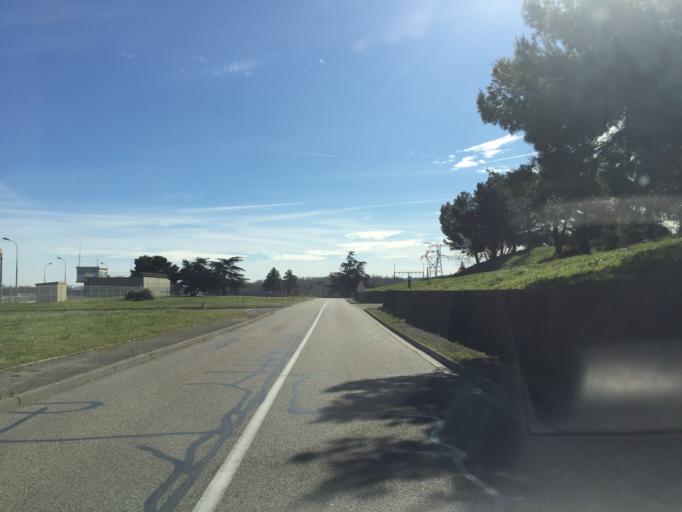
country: FR
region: Languedoc-Roussillon
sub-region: Departement du Gard
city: Saint-Genies-de-Comolas
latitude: 44.0969
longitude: 4.7207
